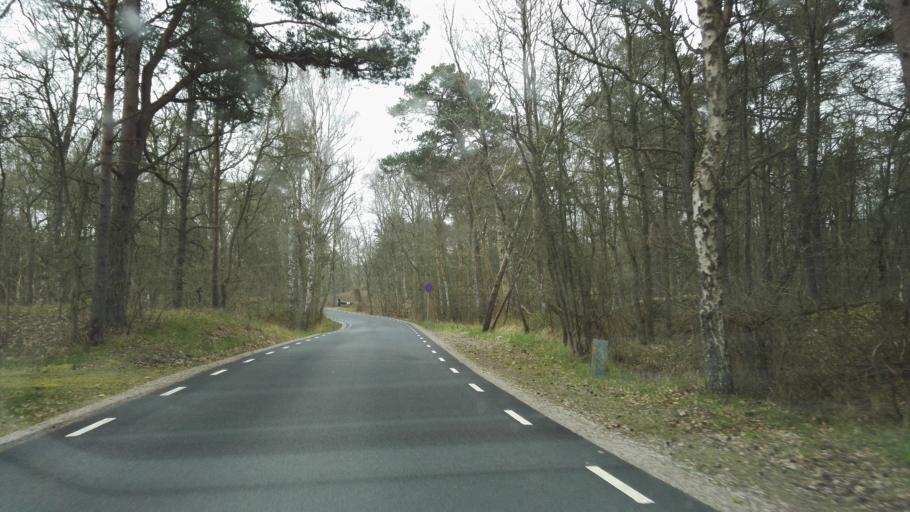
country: SE
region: Skane
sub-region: Simrishamns Kommun
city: Simrishamn
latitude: 55.3896
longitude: 14.1895
